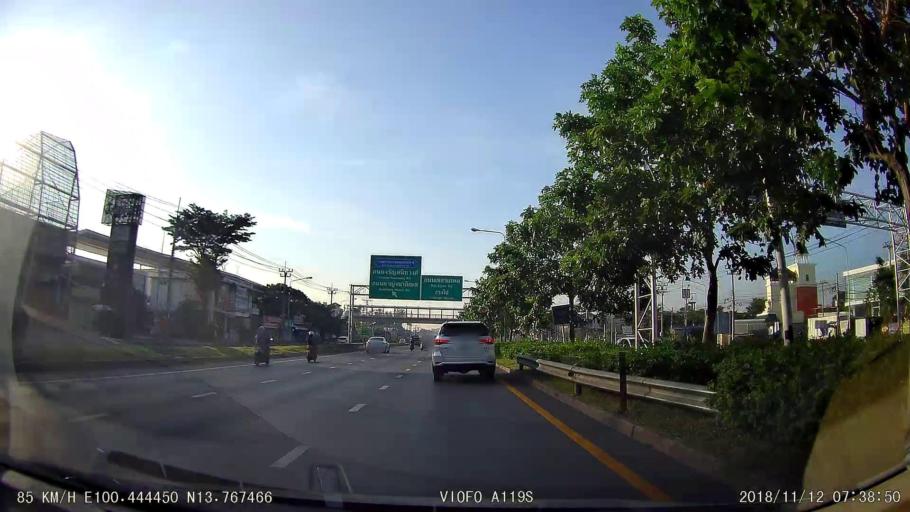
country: TH
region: Bangkok
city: Taling Chan
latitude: 13.7663
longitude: 100.4446
